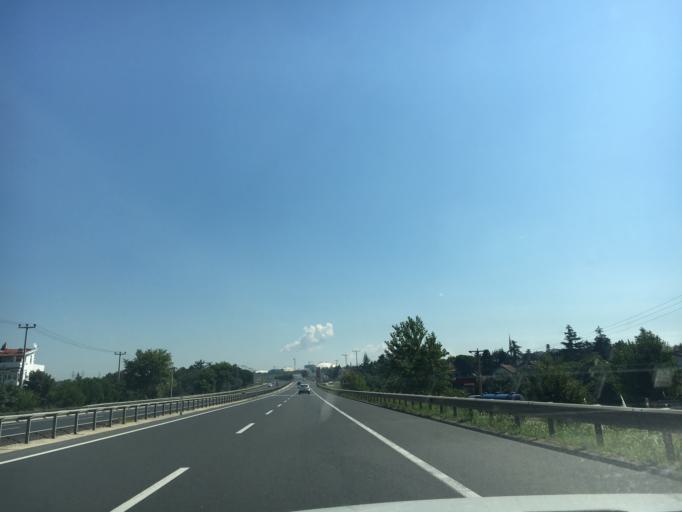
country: TR
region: Tekirdag
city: Marmara Ereglisi
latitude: 40.9843
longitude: 27.9658
